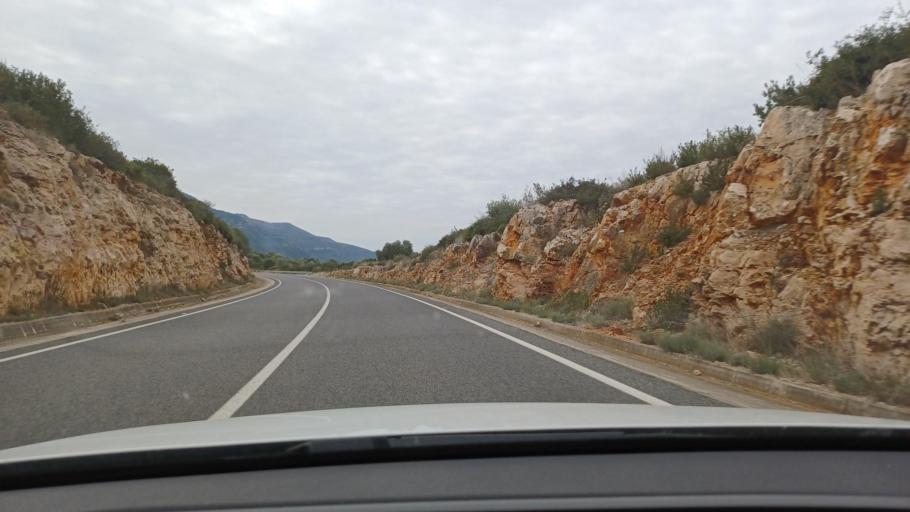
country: ES
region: Catalonia
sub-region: Provincia de Tarragona
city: Masdenverge
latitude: 40.6812
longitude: 0.5252
